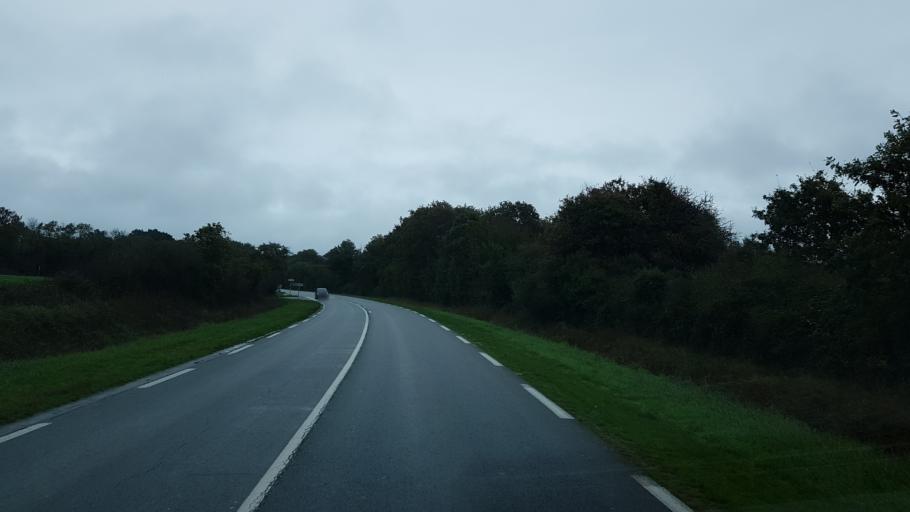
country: FR
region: Brittany
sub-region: Departement du Morbihan
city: Saint-Gildas-de-Rhuys
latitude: 47.5277
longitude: -2.8168
